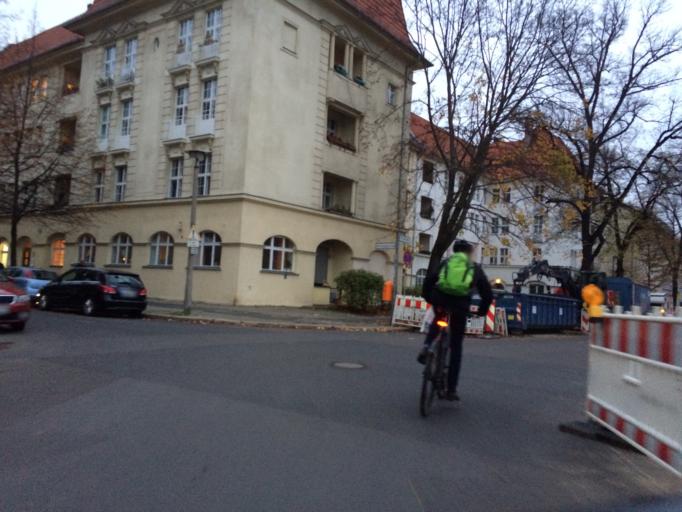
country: DE
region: Berlin
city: Weissensee
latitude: 52.5497
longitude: 13.4541
